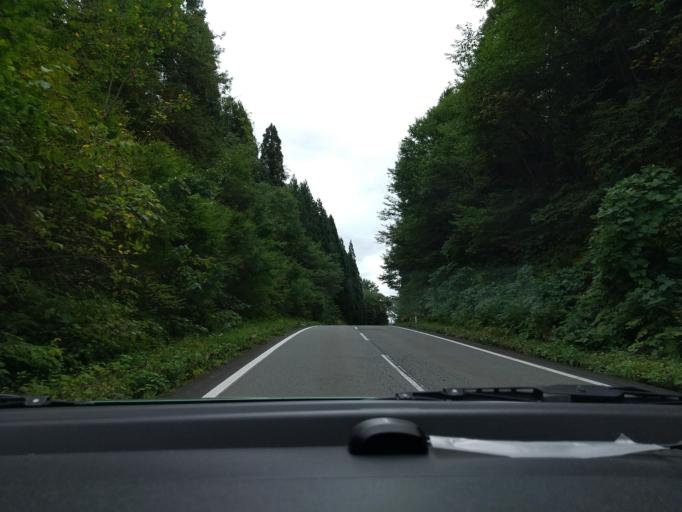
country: JP
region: Akita
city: Kakunodatemachi
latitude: 39.5678
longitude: 140.6369
